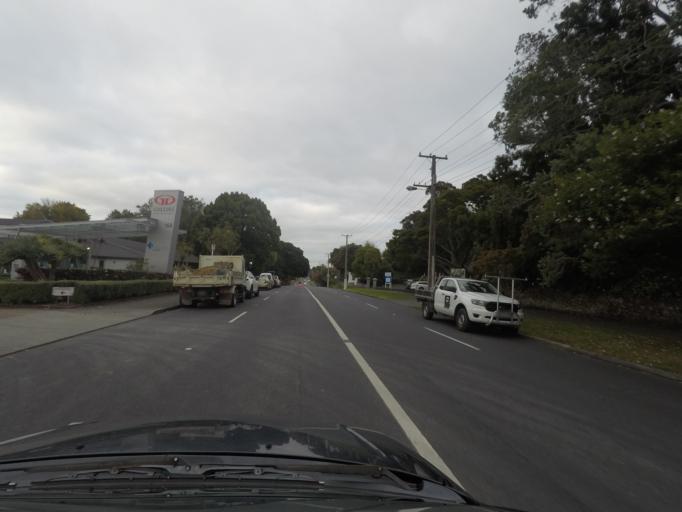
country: NZ
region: Auckland
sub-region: Auckland
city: Auckland
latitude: -36.8808
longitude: 174.7720
